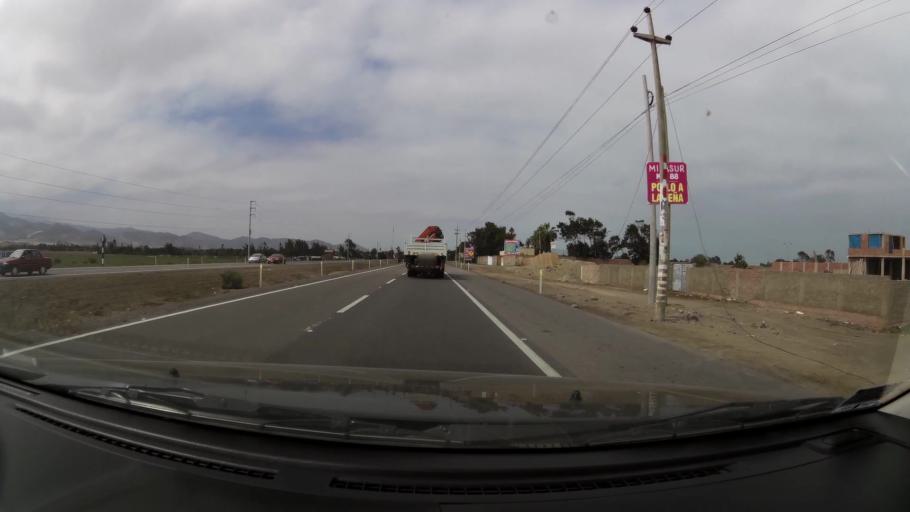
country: PE
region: Lima
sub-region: Provincia de Canete
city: Mala
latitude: -12.6923
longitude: -76.6458
